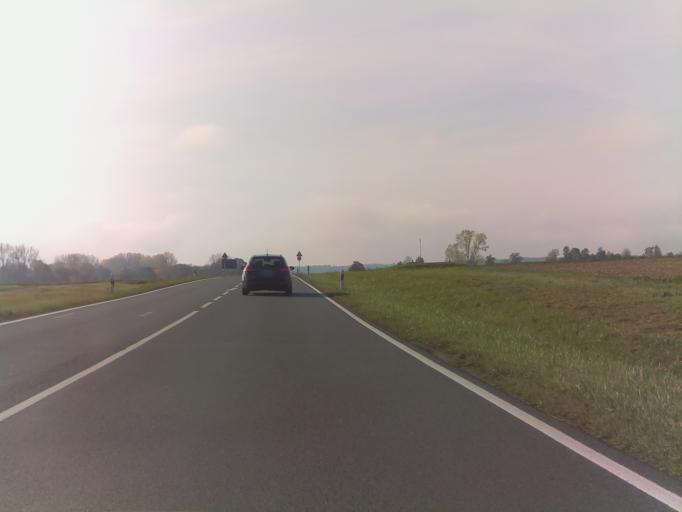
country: DE
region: Bavaria
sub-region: Regierungsbezirk Unterfranken
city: Prichsenstadt
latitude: 49.8272
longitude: 10.3140
